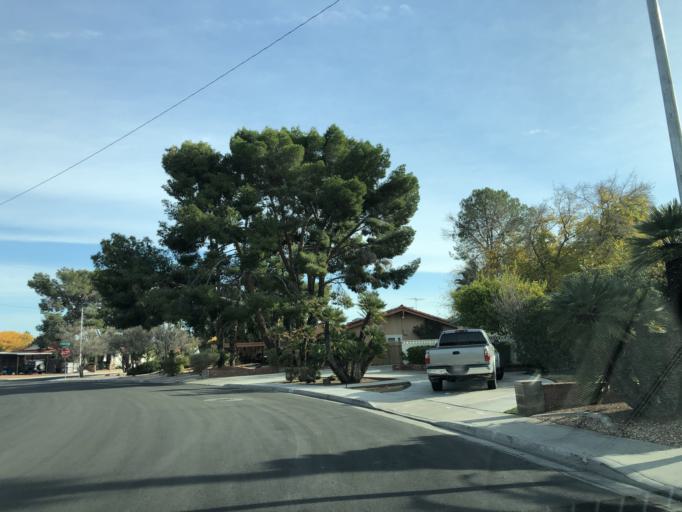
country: US
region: Nevada
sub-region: Clark County
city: Winchester
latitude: 36.1233
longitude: -115.1220
